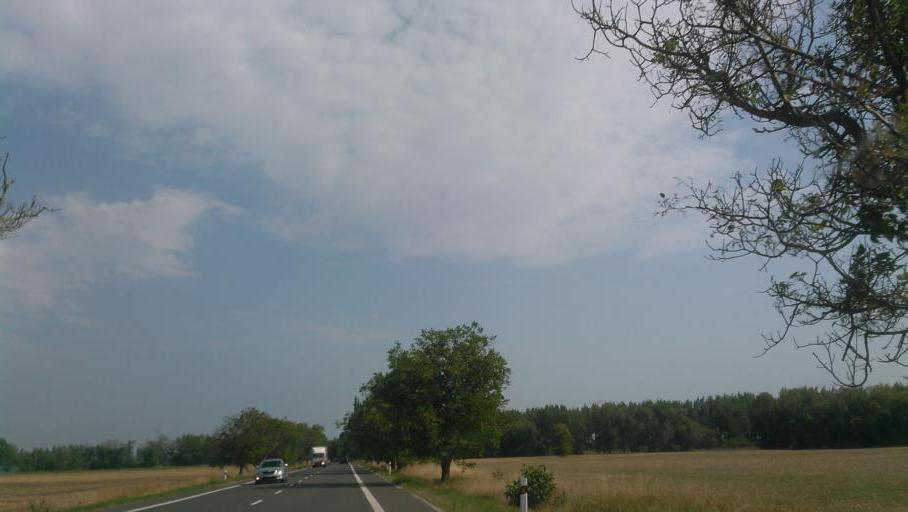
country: SK
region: Trnavsky
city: Dunajska Streda
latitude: 47.9521
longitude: 17.7057
